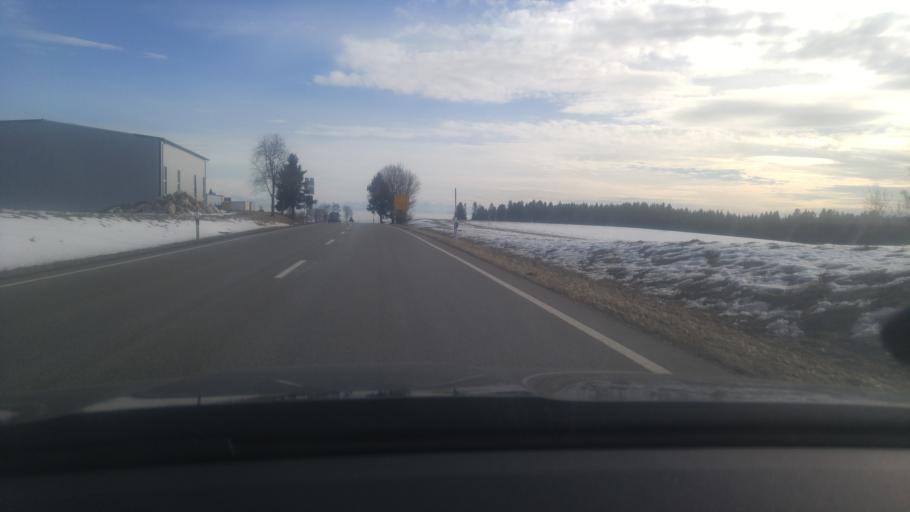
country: DE
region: Baden-Wuerttemberg
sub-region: Freiburg Region
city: Hochenschwand
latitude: 47.7076
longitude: 8.1434
